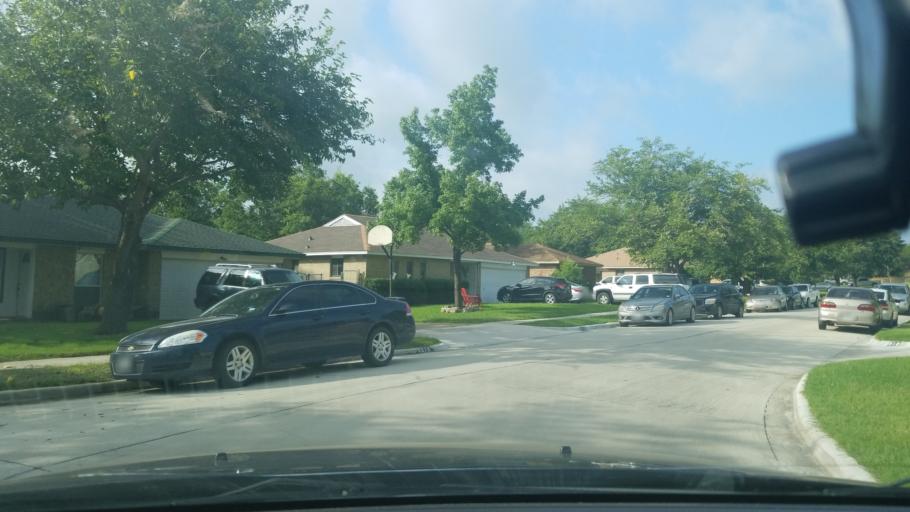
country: US
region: Texas
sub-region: Dallas County
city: Mesquite
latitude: 32.7738
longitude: -96.6366
